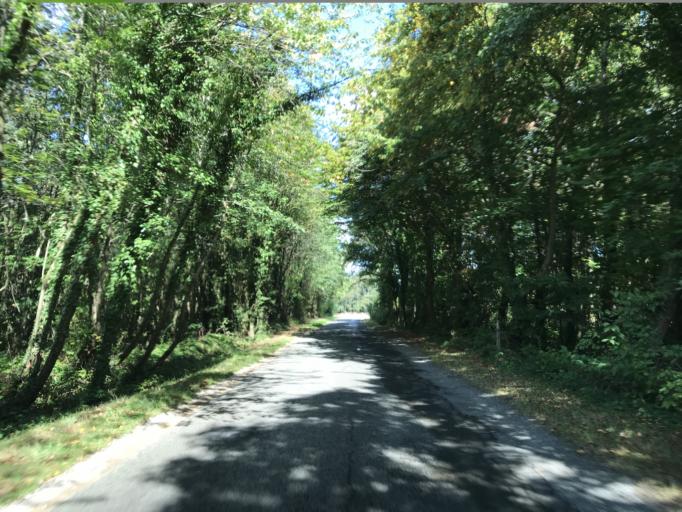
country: FR
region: Haute-Normandie
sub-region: Departement de l'Eure
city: La Chapelle-Reanville
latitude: 49.0982
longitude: 1.3903
